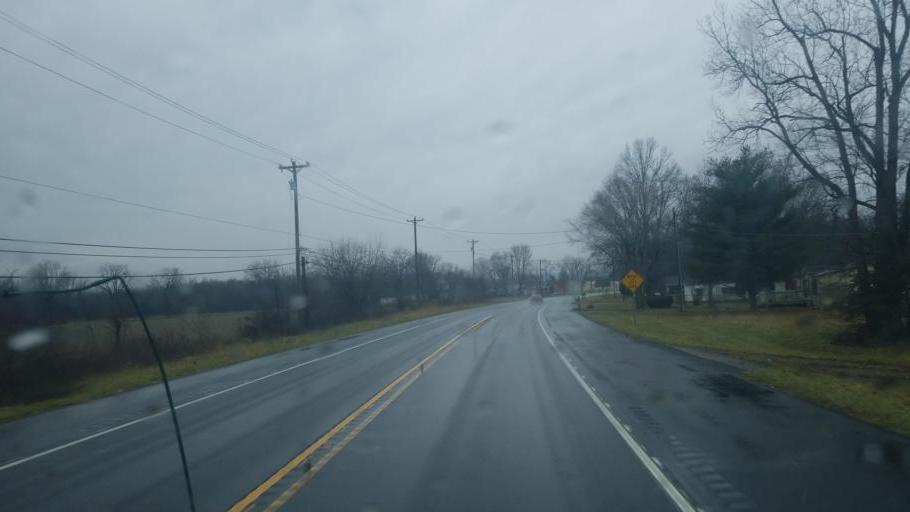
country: US
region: Indiana
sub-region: Bartholomew County
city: Columbus
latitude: 39.1971
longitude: -85.9907
